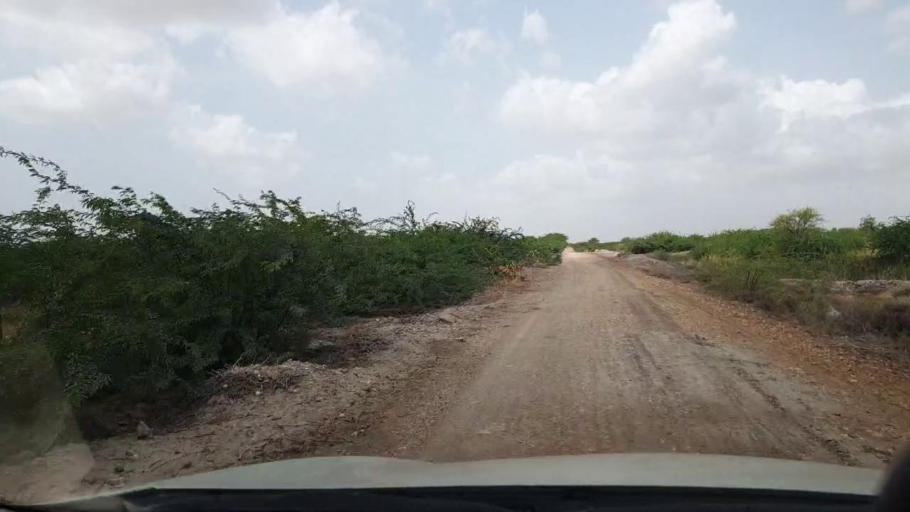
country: PK
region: Sindh
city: Kadhan
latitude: 24.3700
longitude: 68.8531
